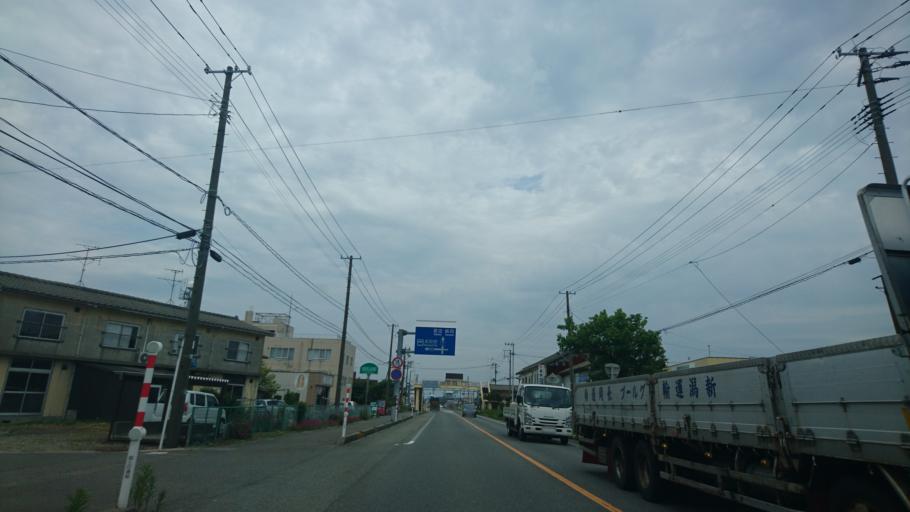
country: JP
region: Niigata
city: Murakami
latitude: 38.1165
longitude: 139.4509
